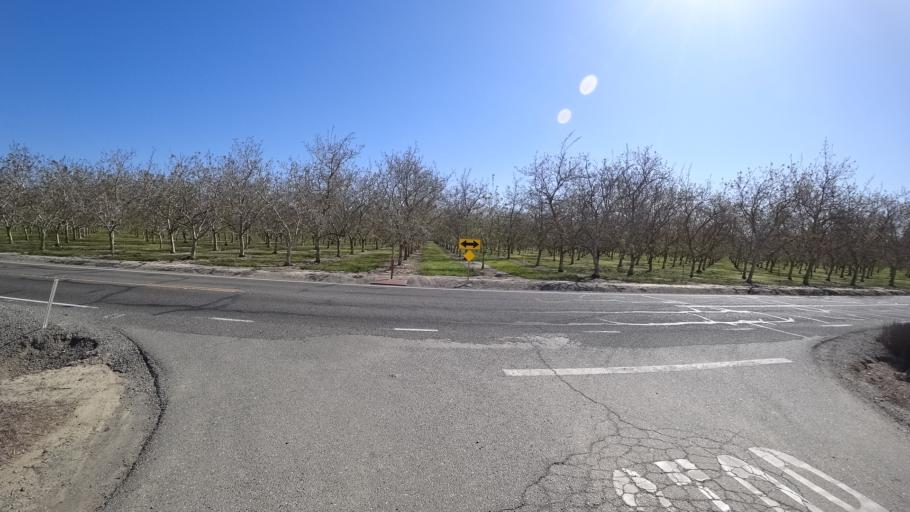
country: US
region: California
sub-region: Glenn County
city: Hamilton City
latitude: 39.7174
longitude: -122.0073
